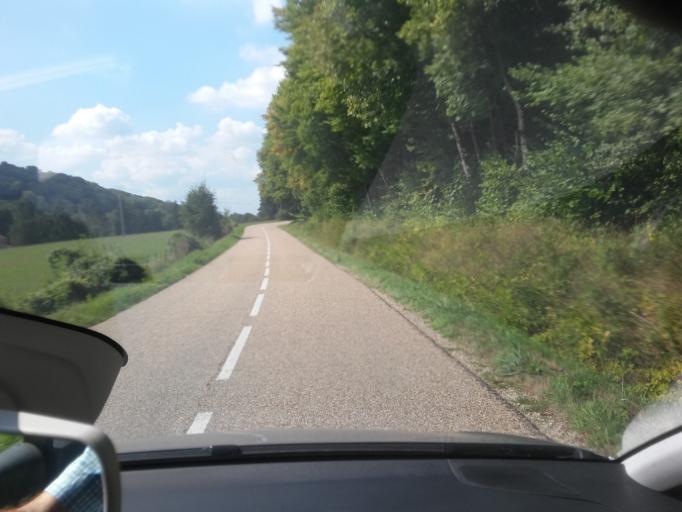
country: FR
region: Lorraine
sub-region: Departement de Meurthe-et-Moselle
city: Longuyon
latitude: 49.4976
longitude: 5.5561
